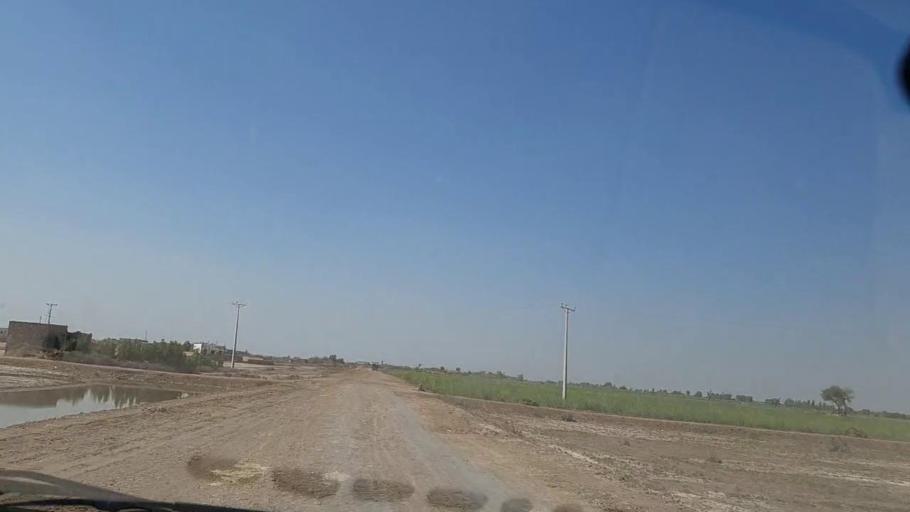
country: PK
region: Sindh
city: Mirwah Gorchani
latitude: 25.3789
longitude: 69.0078
